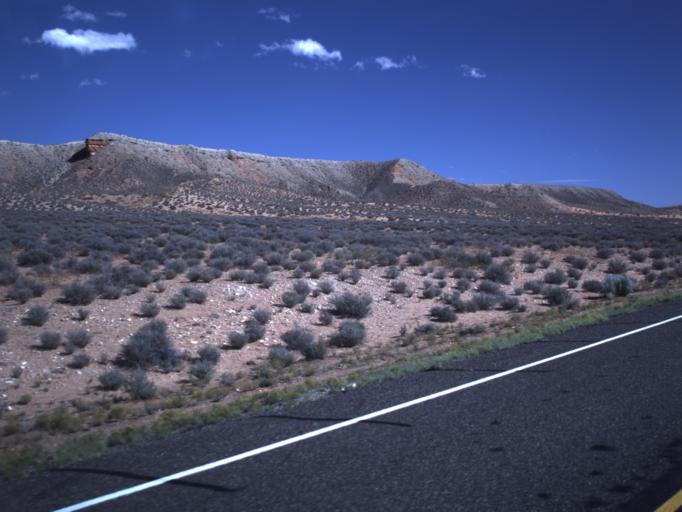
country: US
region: Utah
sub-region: Wayne County
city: Loa
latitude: 38.0885
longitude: -110.6168
